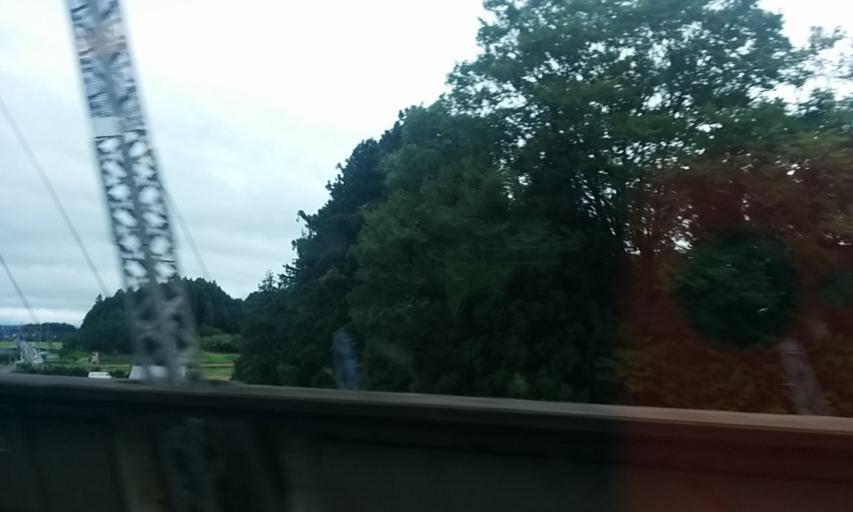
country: JP
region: Tochigi
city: Yaita
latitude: 36.8200
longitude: 139.9594
